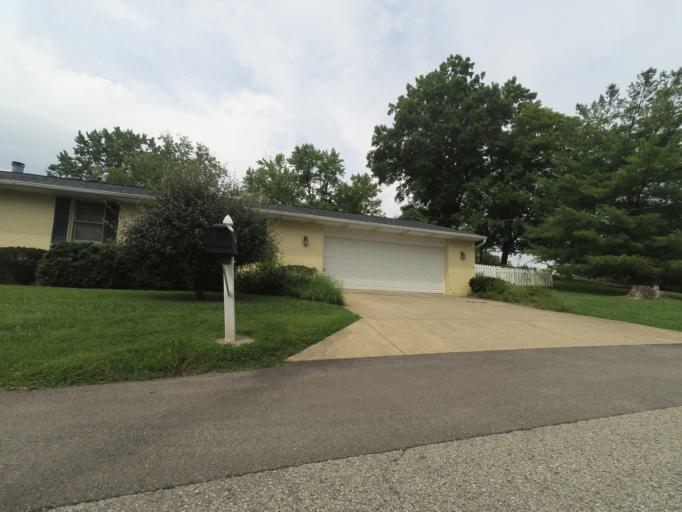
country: US
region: West Virginia
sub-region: Cabell County
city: Huntington
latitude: 38.3961
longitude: -82.4375
